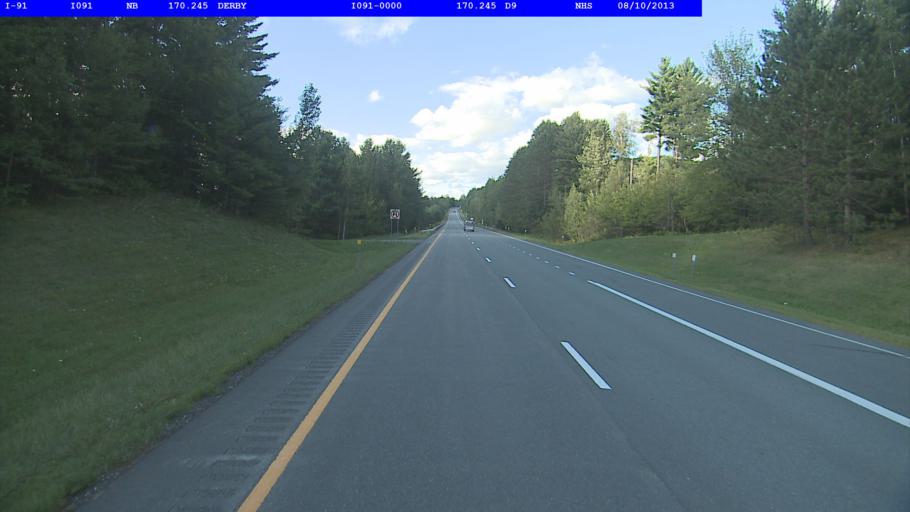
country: US
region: Vermont
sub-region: Orleans County
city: Newport
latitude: 44.9252
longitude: -72.1714
